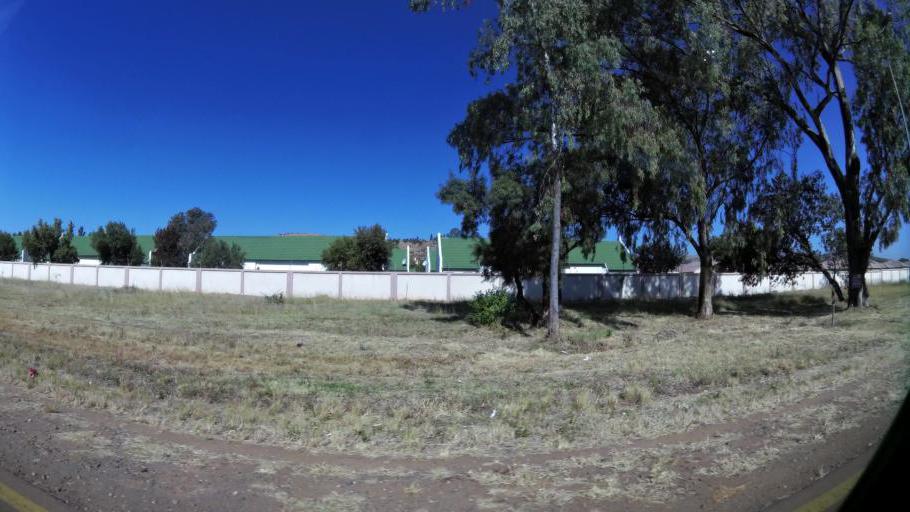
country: ZA
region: North-West
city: Ga-Rankuwa
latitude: -25.6681
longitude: 28.0825
